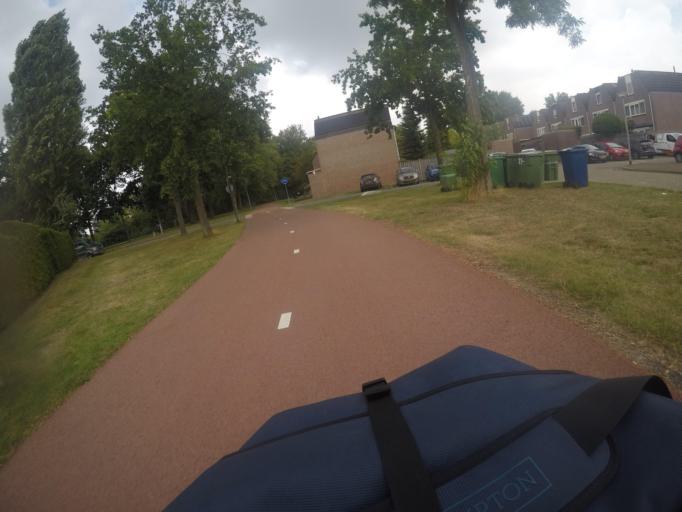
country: NL
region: Flevoland
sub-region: Gemeente Almere
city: Almere Stad
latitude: 52.3428
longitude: 5.2184
